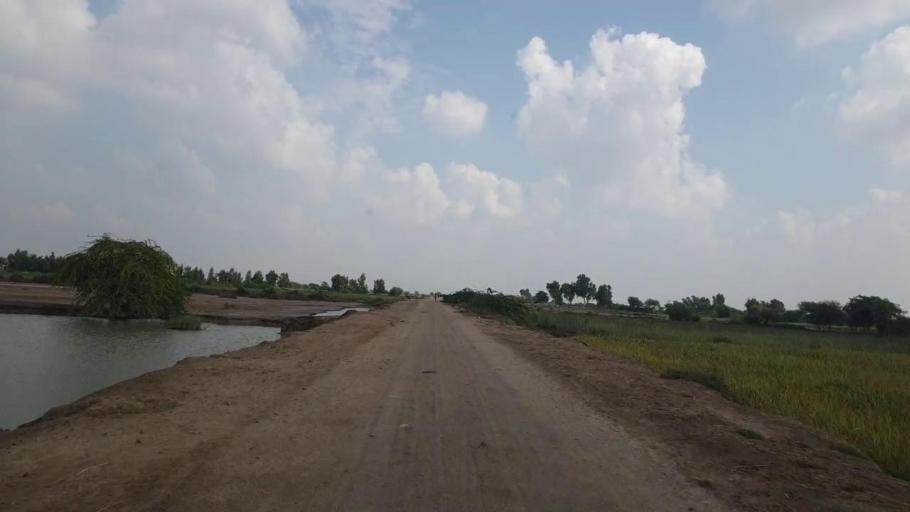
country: PK
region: Sindh
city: Badin
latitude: 24.5328
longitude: 68.6123
